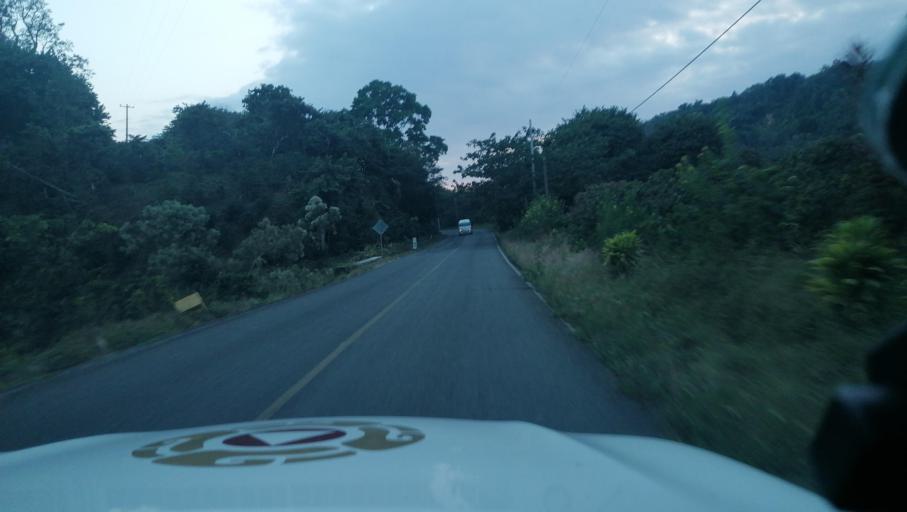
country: MX
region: Chiapas
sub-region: Cacahoatan
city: Benito Juarez
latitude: 15.0467
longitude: -92.2437
